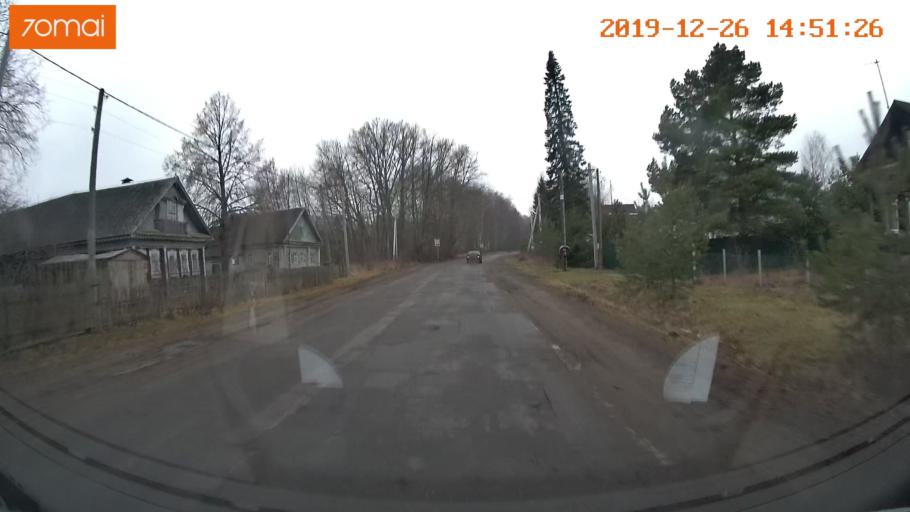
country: RU
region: Jaroslavl
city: Poshekhon'ye
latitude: 58.3258
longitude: 38.9110
